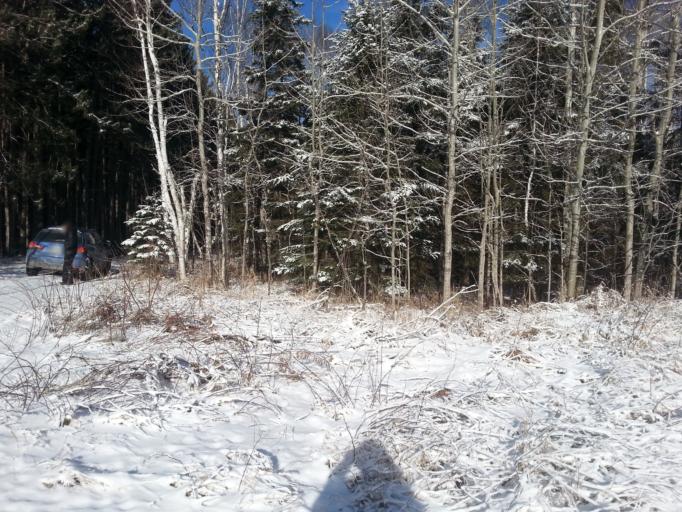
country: CA
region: Ontario
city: Greater Sudbury
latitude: 45.9136
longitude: -80.5713
